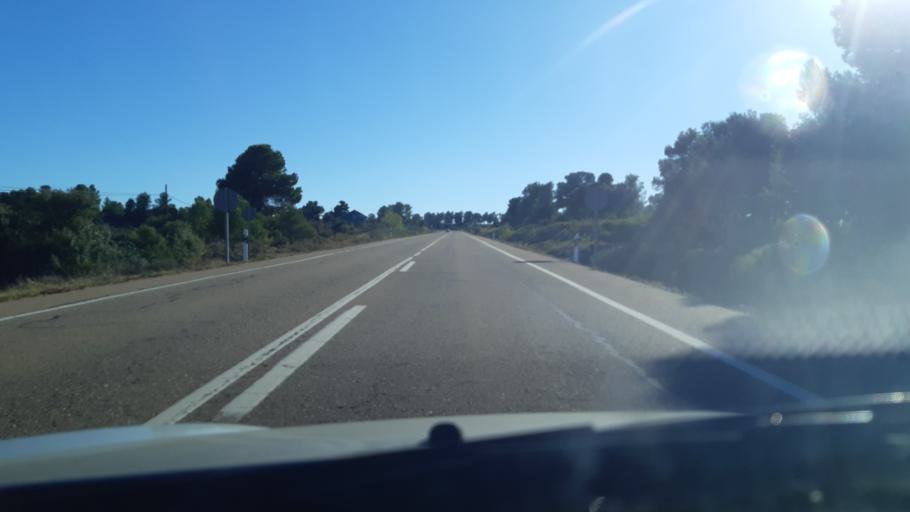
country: ES
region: Aragon
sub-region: Provincia de Teruel
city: Valjunquera
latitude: 40.9468
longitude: -0.0107
